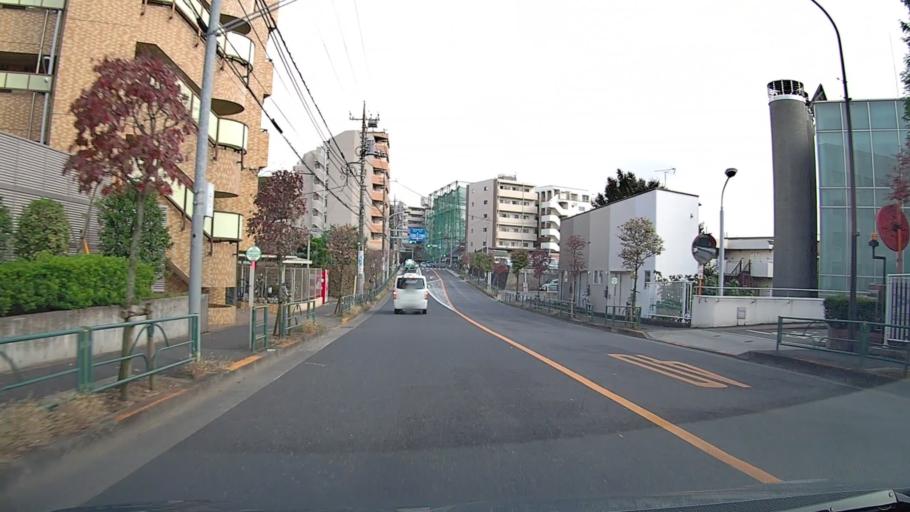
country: JP
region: Tokyo
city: Musashino
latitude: 35.7310
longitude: 139.5902
